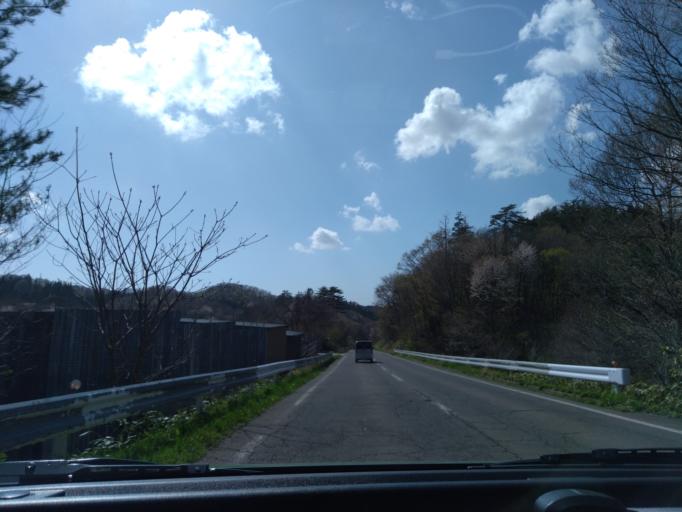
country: JP
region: Akita
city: Akita
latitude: 39.6935
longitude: 140.2439
